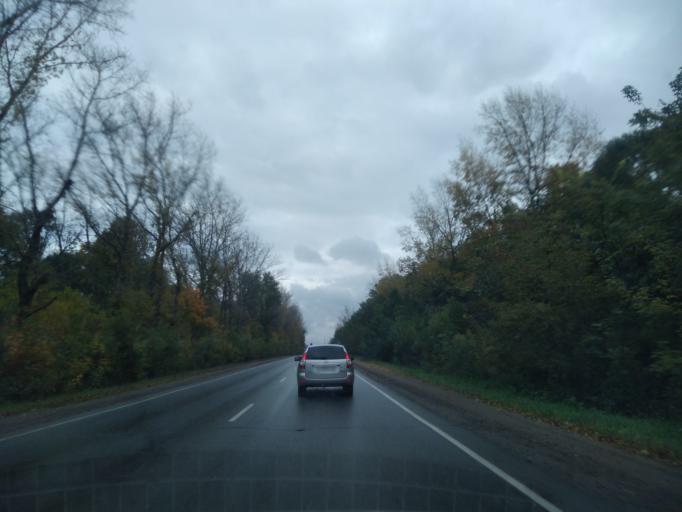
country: RU
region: Tula
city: Yefremov
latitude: 53.1556
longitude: 38.0389
